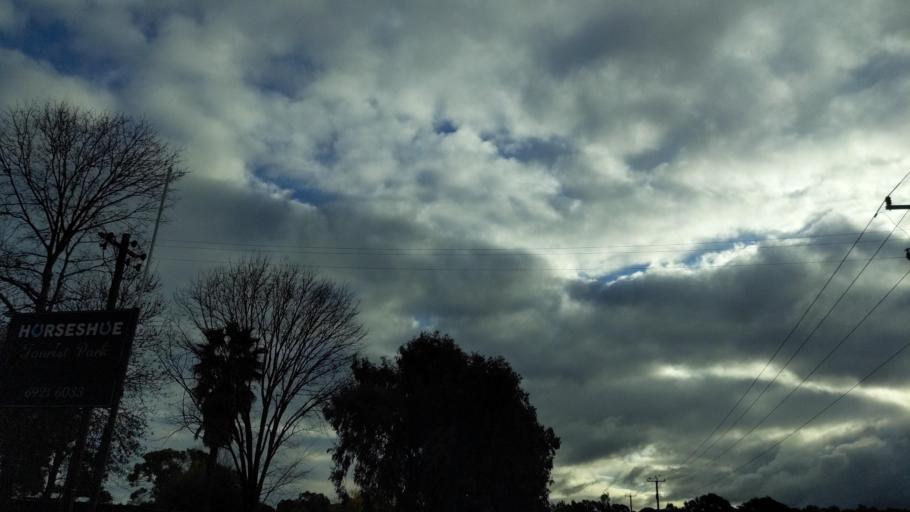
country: AU
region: New South Wales
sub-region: Wagga Wagga
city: Wagga Wagga
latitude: -35.0694
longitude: 147.3865
